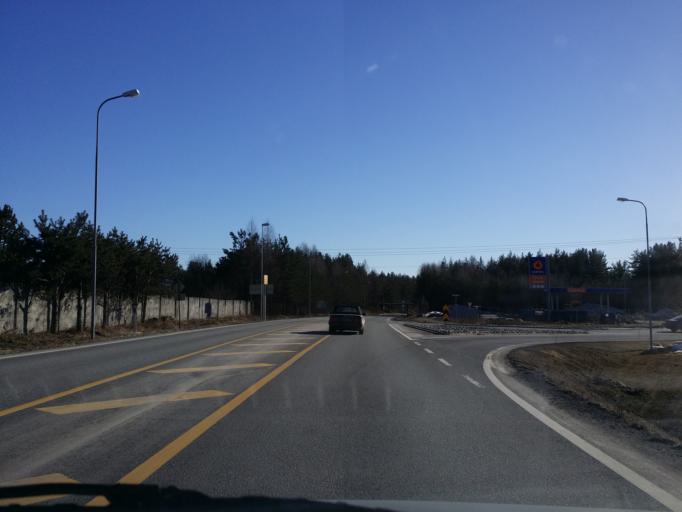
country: NO
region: Buskerud
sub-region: Ringerike
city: Honefoss
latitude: 60.2215
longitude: 10.2579
